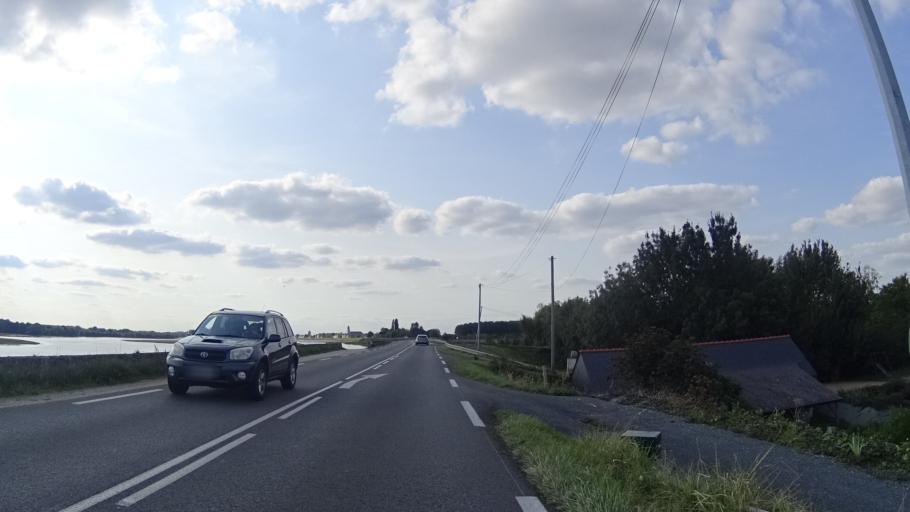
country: FR
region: Pays de la Loire
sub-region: Departement de Maine-et-Loire
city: Blaison-Gohier
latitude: 47.4174
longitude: -0.3685
